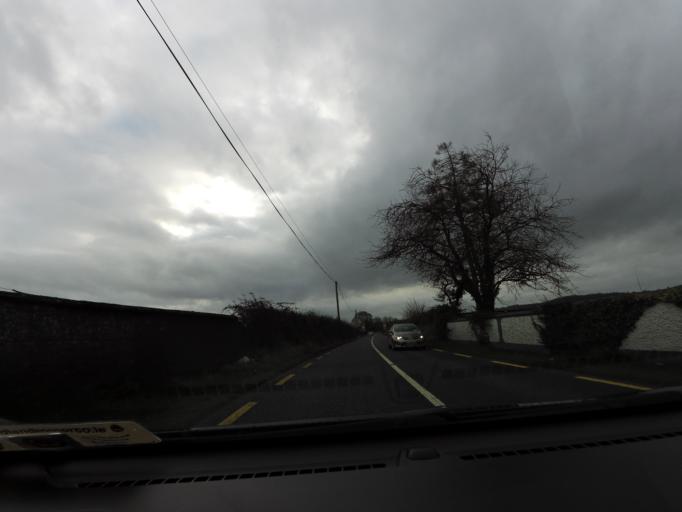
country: IE
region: Leinster
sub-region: Kilkenny
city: Kilkenny
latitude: 52.7180
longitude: -7.2933
